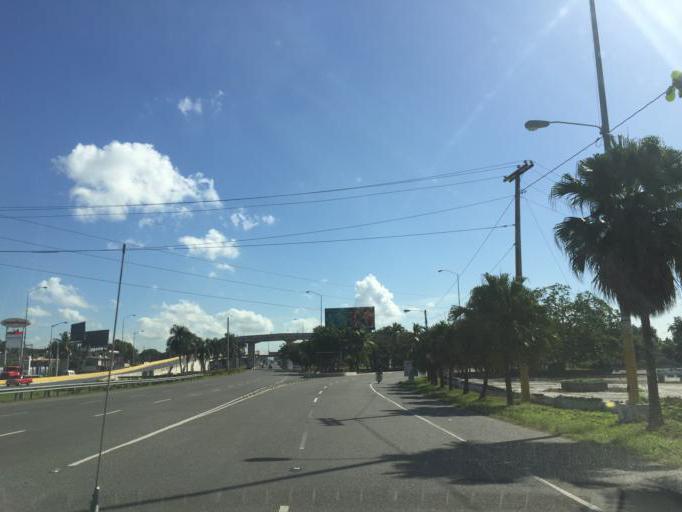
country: DO
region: Santo Domingo
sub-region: Santo Domingo
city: Boca Chica
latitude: 18.4505
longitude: -69.6841
